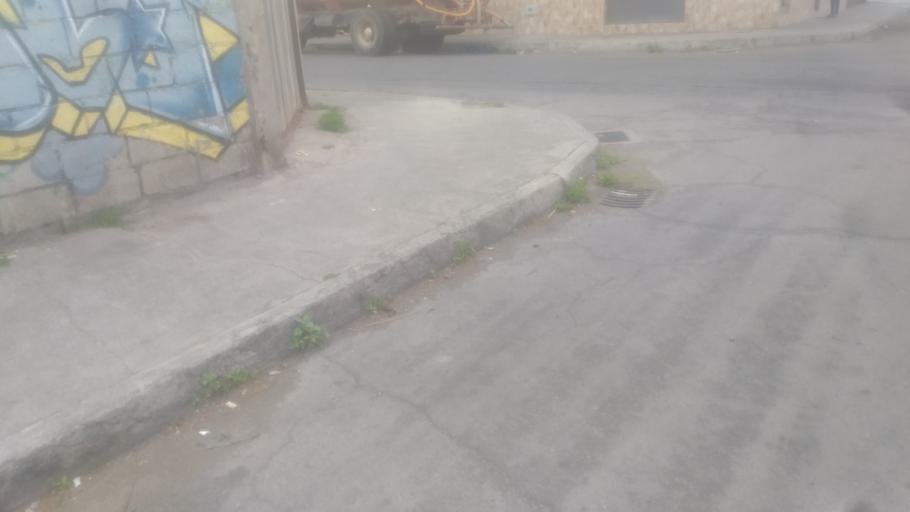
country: EC
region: Chimborazo
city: Riobamba
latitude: -1.6647
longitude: -78.6469
